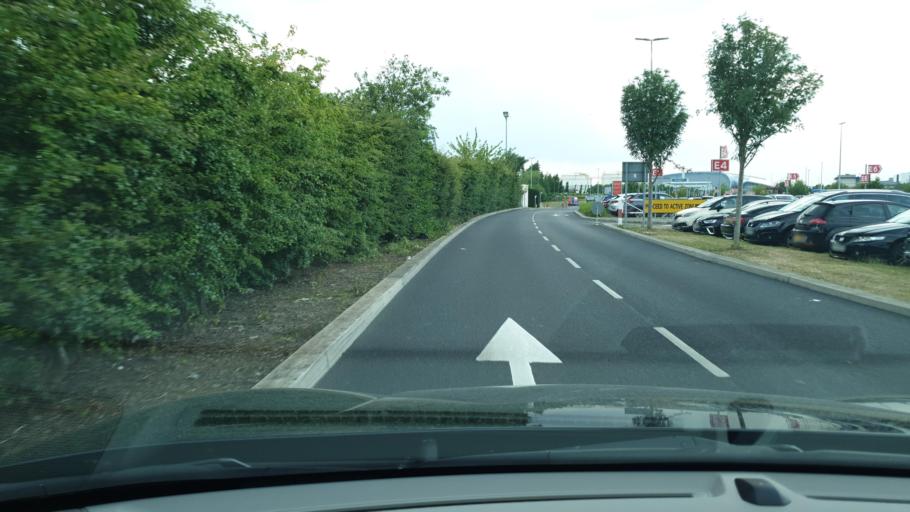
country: IE
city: Bonnybrook
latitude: 53.4221
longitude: -6.2242
